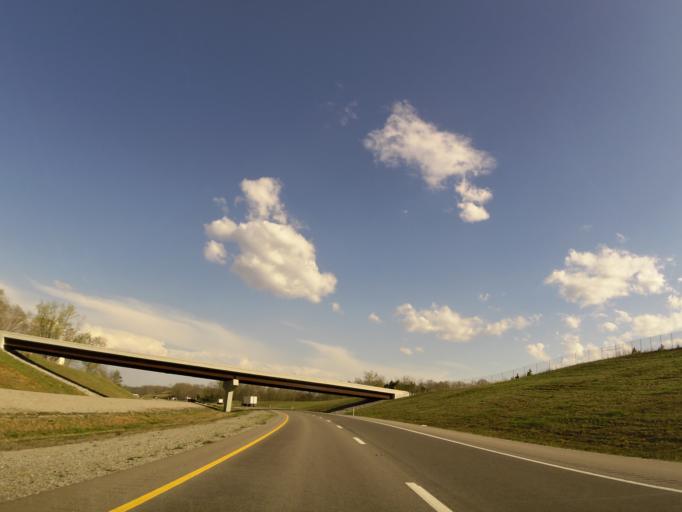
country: US
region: Tennessee
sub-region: Williamson County
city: Fairview
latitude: 35.8647
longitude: -87.0887
